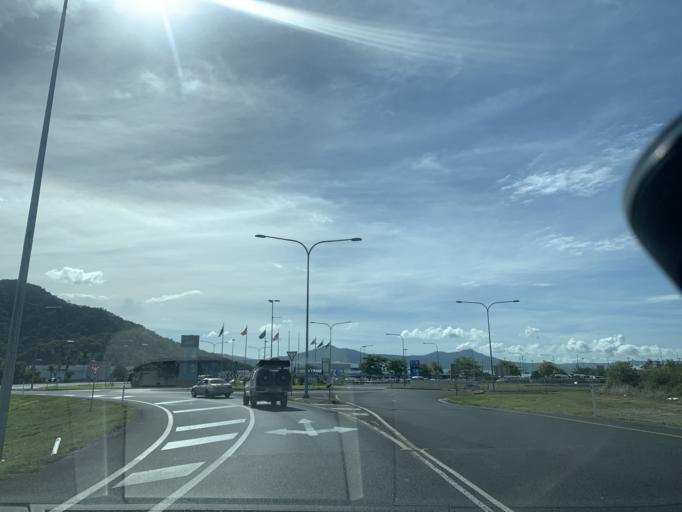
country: AU
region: Queensland
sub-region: Cairns
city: Cairns
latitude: -16.8791
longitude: 145.7578
